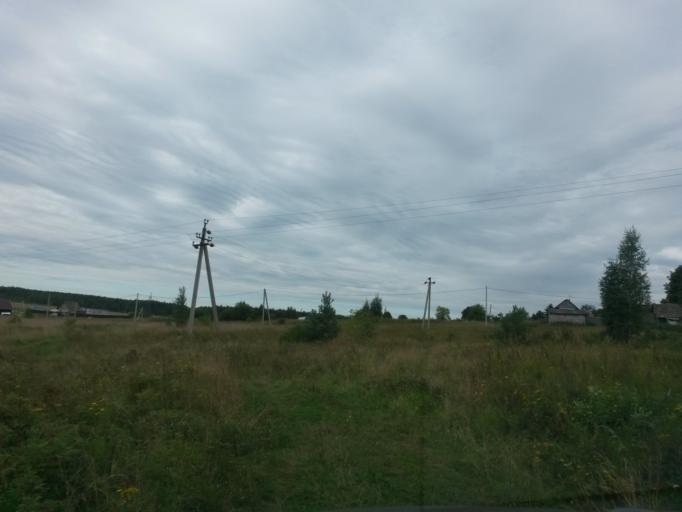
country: RU
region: Jaroslavl
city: Gavrilov-Yam
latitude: 57.3077
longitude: 39.9518
